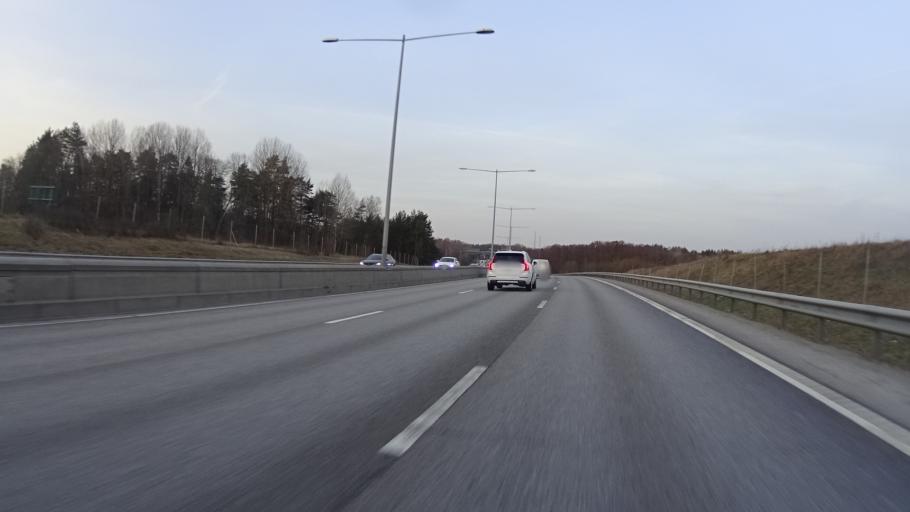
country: SE
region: Stockholm
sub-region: Botkyrka Kommun
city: Eriksberg
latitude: 59.2371
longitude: 17.8141
